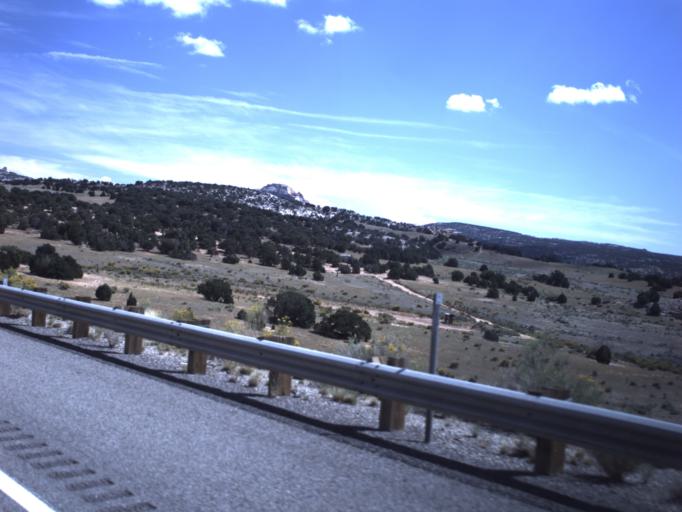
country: US
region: Utah
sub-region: Emery County
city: Ferron
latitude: 38.8468
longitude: -110.8951
